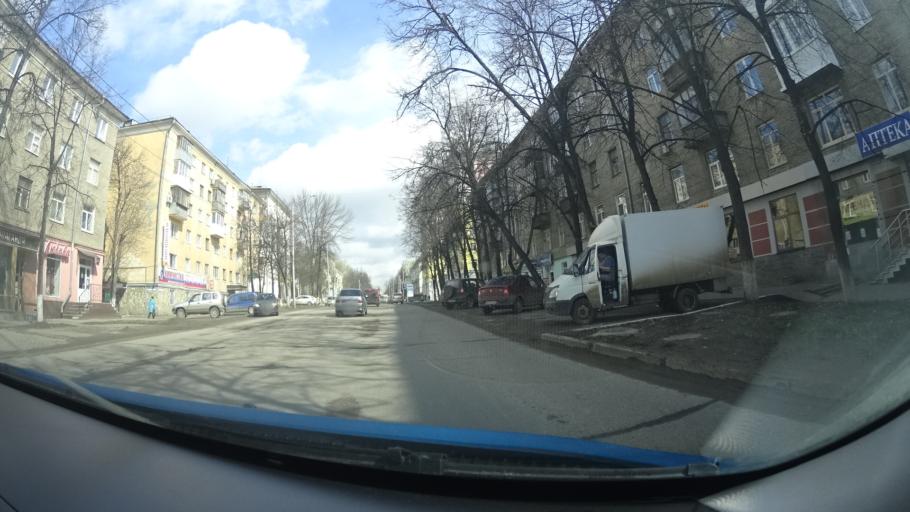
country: RU
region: Bashkortostan
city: Ufa
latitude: 54.8164
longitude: 56.0739
